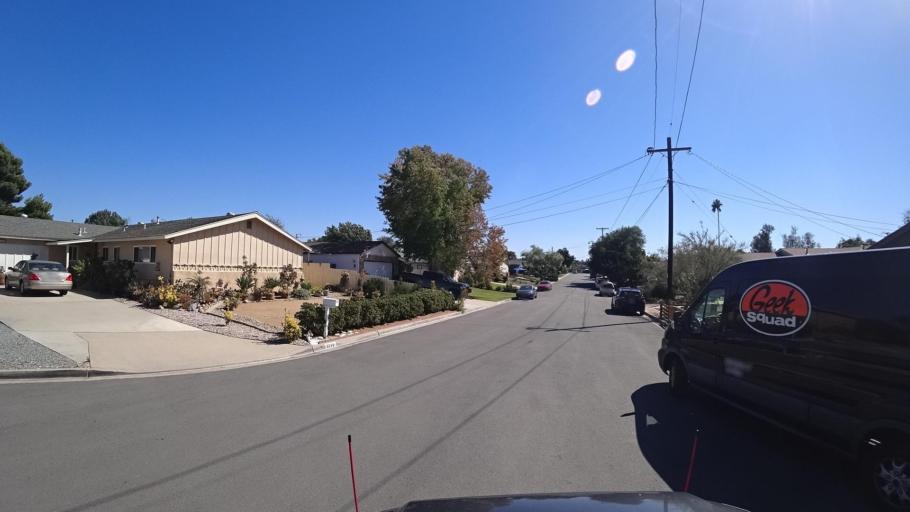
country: US
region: California
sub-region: San Diego County
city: Bonita
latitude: 32.6574
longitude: -117.0561
